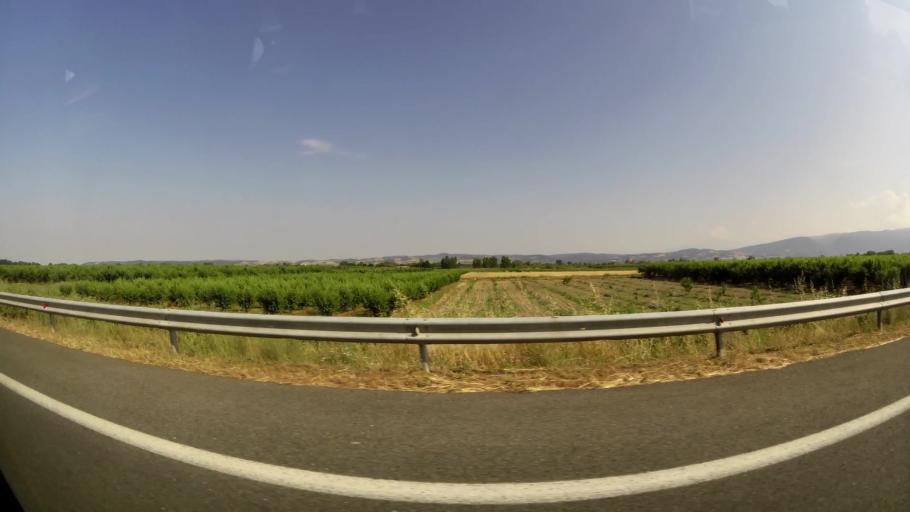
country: GR
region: Central Macedonia
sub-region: Nomos Imathias
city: Loutros
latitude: 40.5679
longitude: 22.3796
